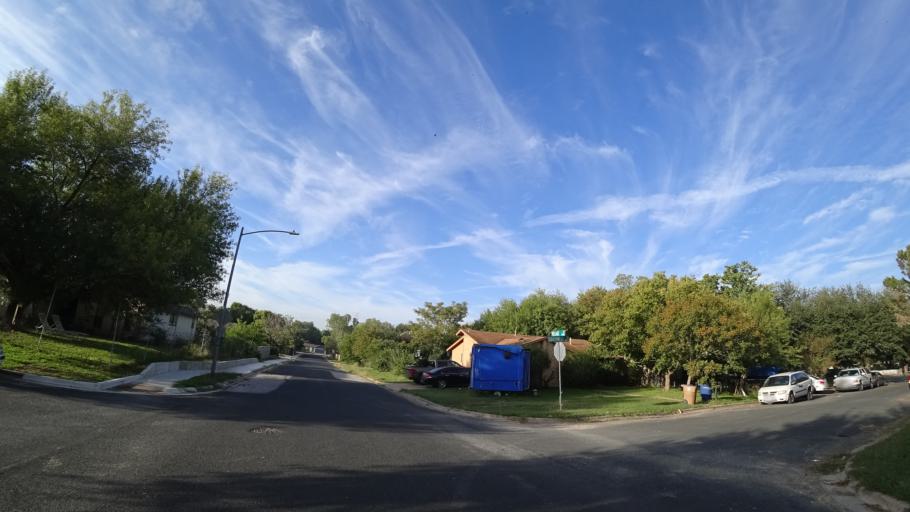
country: US
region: Texas
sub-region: Travis County
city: Onion Creek
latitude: 30.1927
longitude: -97.7461
